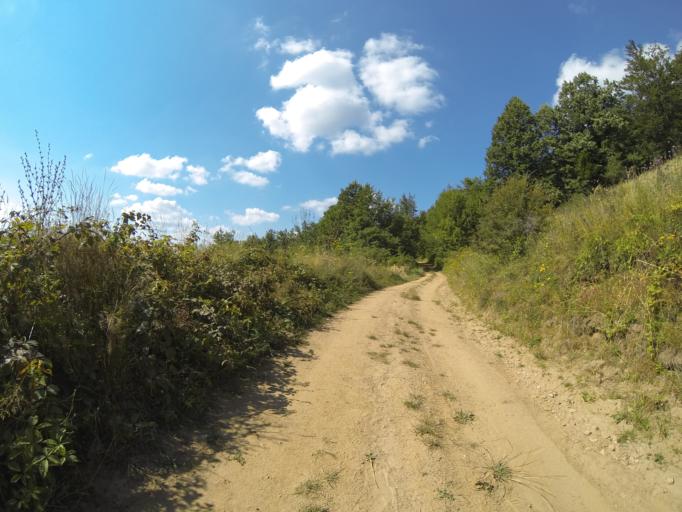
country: RO
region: Mehedinti
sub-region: Comuna Svinita
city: Svinita
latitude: 44.5639
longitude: 22.1366
